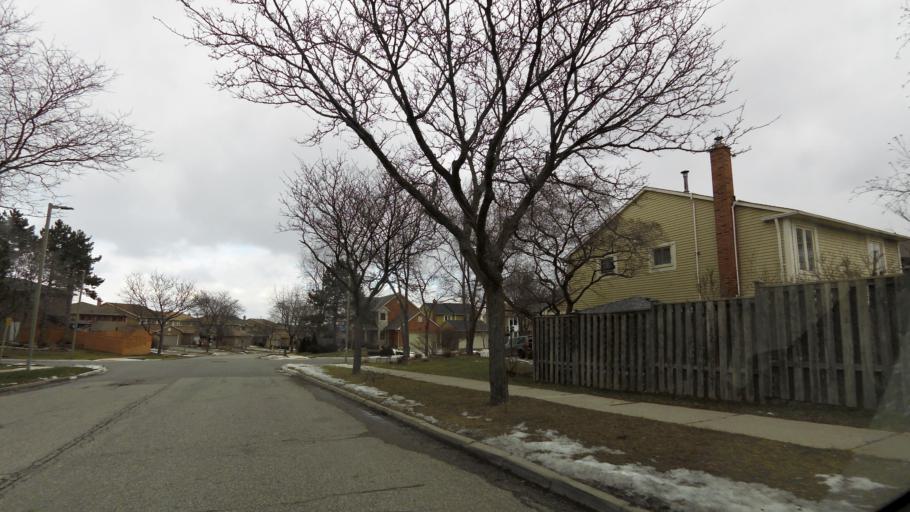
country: CA
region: Ontario
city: Mississauga
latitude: 43.5551
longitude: -79.6908
